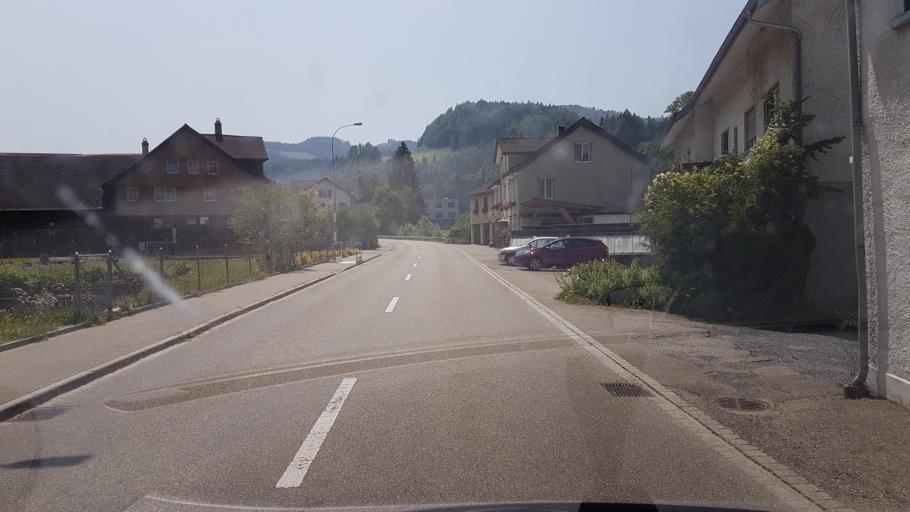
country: CH
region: Saint Gallen
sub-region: Wahlkreis Toggenburg
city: Mogelsberg
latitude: 47.3512
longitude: 9.1297
